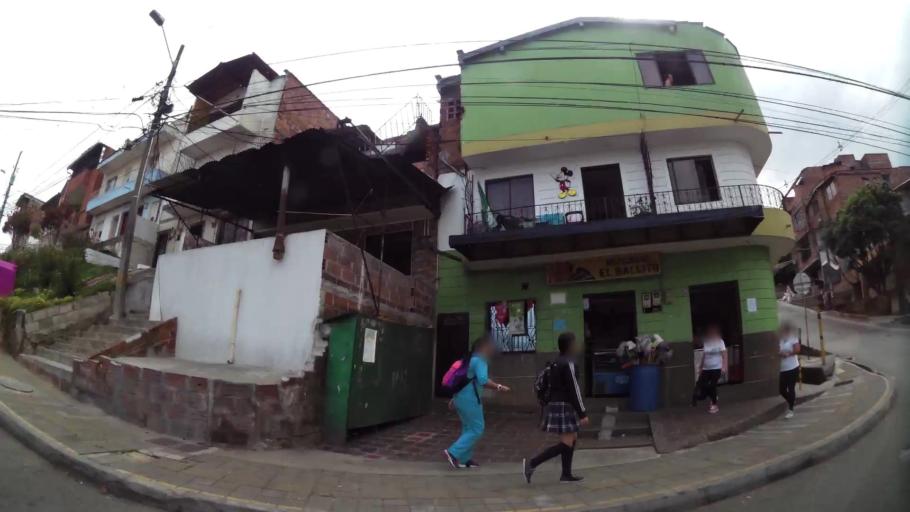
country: CO
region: Antioquia
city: Medellin
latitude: 6.2830
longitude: -75.5519
